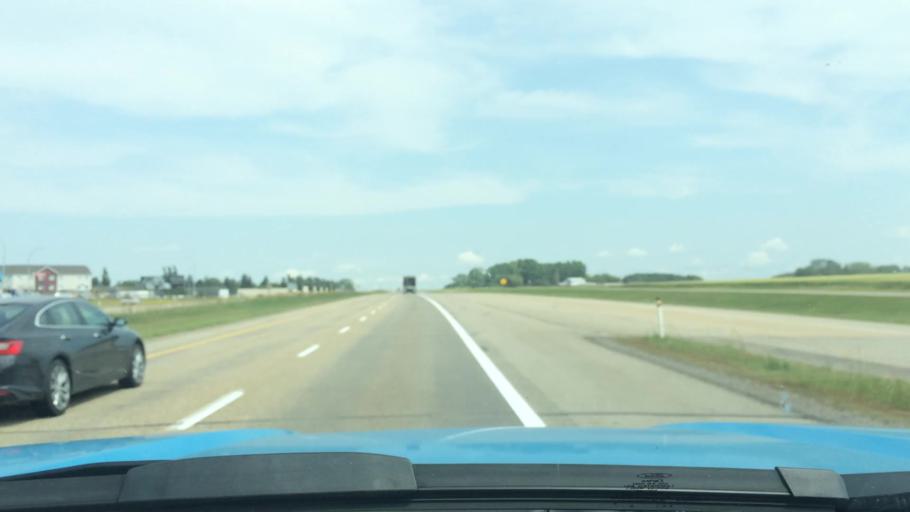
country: CA
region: Alberta
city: Penhold
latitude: 52.0061
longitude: -113.9566
